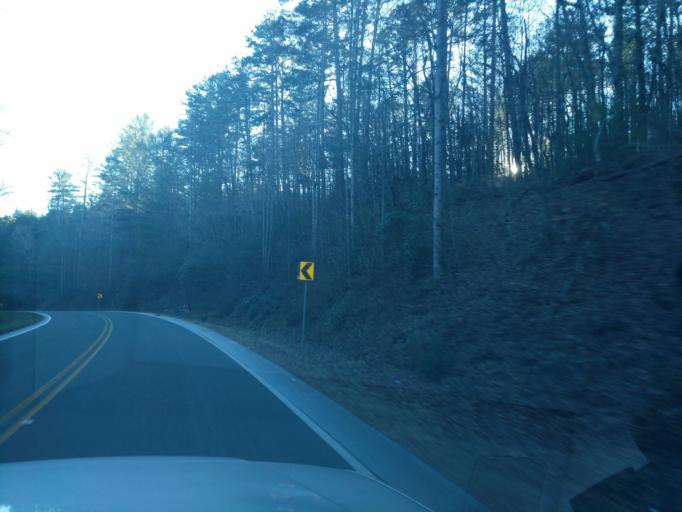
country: US
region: Georgia
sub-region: Rabun County
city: Clayton
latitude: 34.8165
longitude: -83.3191
